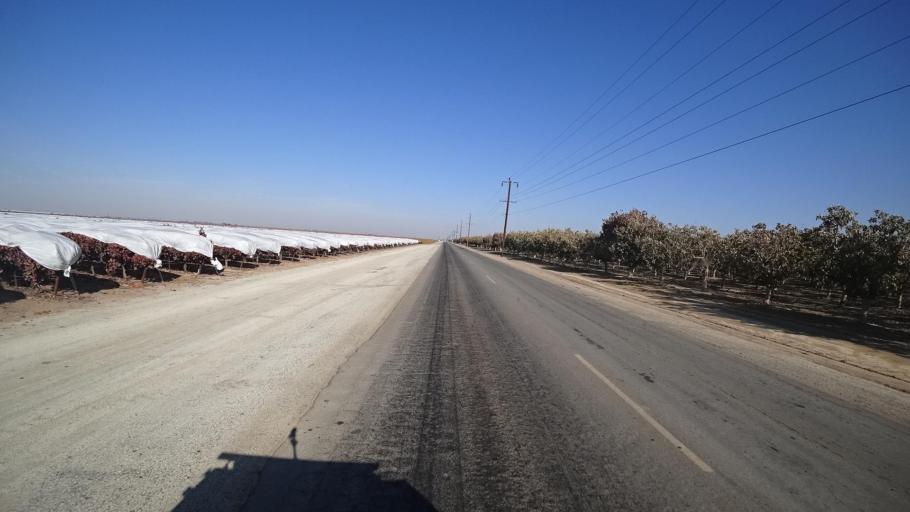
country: US
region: California
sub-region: Kern County
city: McFarland
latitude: 35.7202
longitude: -119.2051
